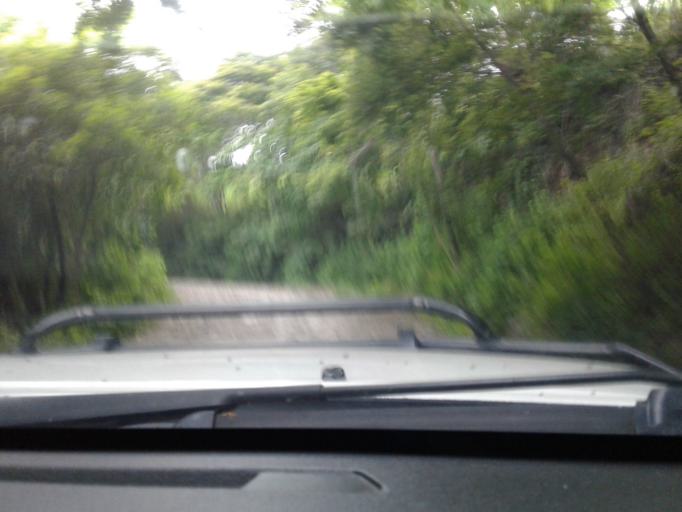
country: NI
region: Leon
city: Santa Rosa del Penon
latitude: 12.9015
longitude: -86.2299
